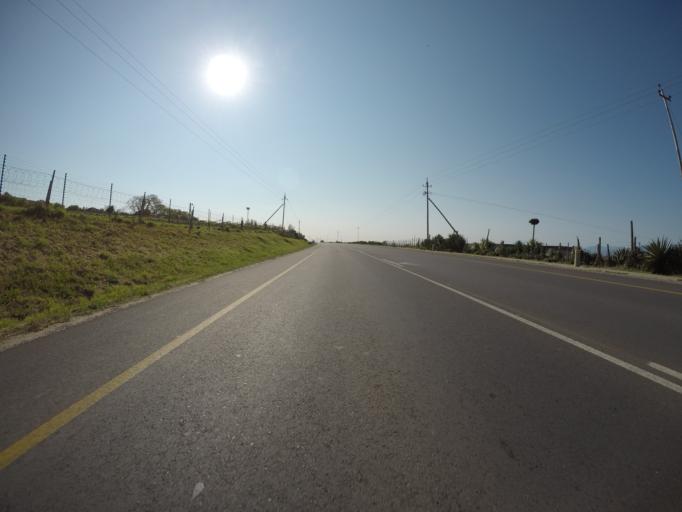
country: ZA
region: Western Cape
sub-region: Cape Winelands District Municipality
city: Noorder-Paarl
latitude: -33.6827
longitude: 18.9466
